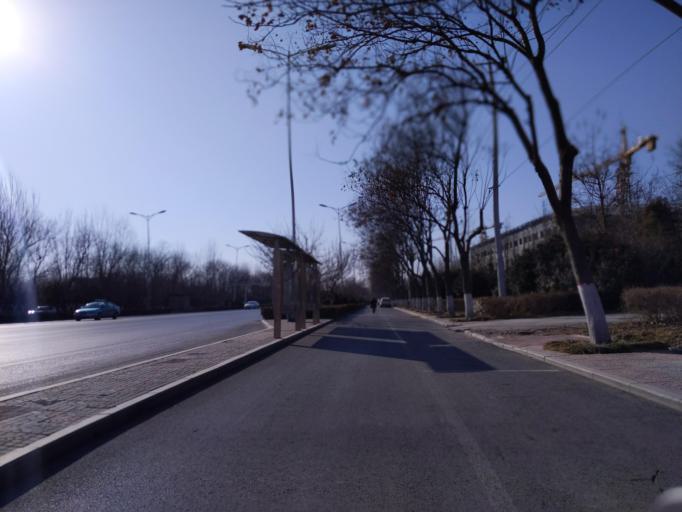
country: CN
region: Henan Sheng
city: Puyang
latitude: 35.7741
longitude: 114.9988
